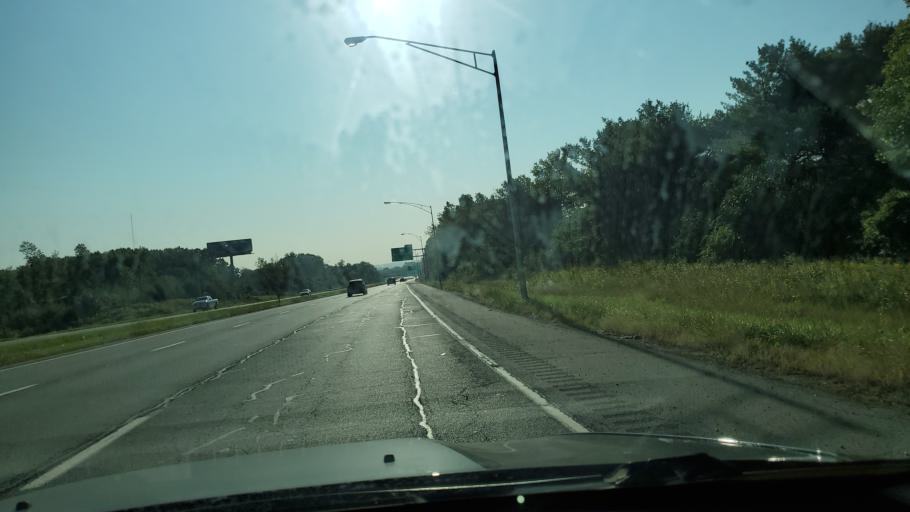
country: US
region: Ohio
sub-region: Trumbull County
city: Girard
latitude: 41.1216
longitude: -80.7058
